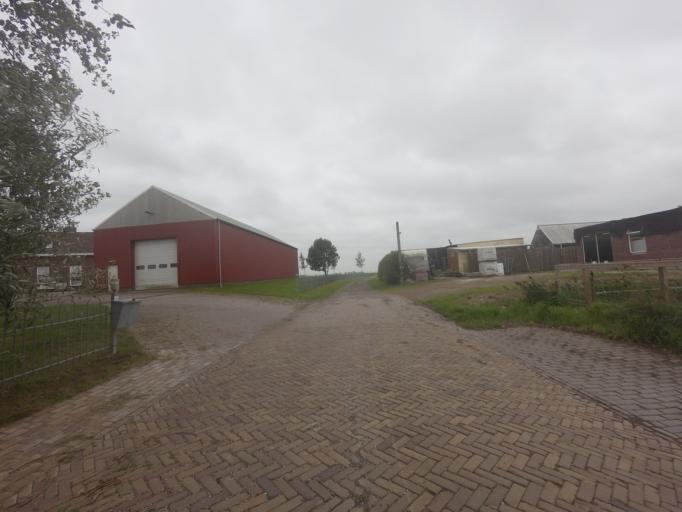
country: NL
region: Friesland
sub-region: Gemeente Ferwerderadiel
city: Ferwert
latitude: 53.3489
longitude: 5.8613
